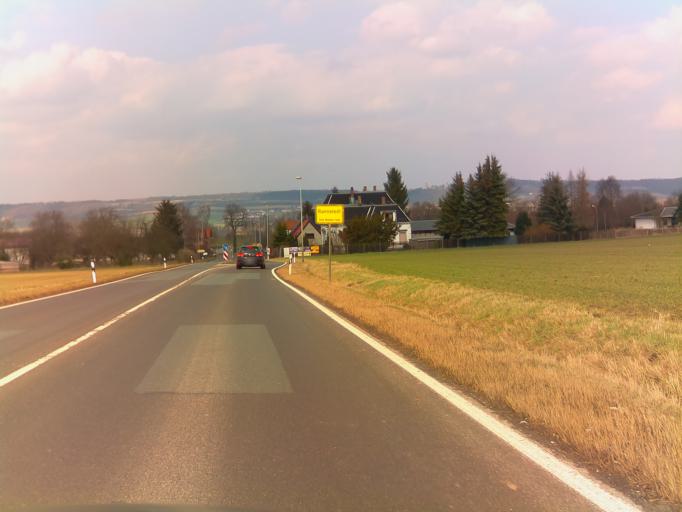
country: DE
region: Thuringia
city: Rannstedt
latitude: 51.0825
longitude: 11.5373
